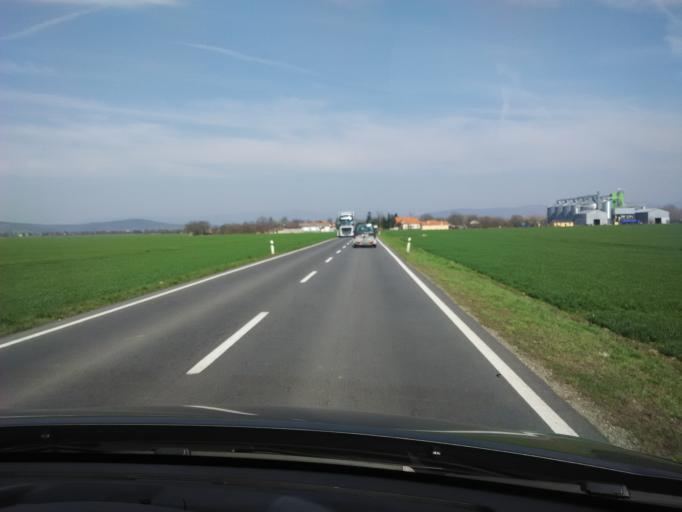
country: SK
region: Nitriansky
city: Tlmace
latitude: 48.2282
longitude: 18.5203
